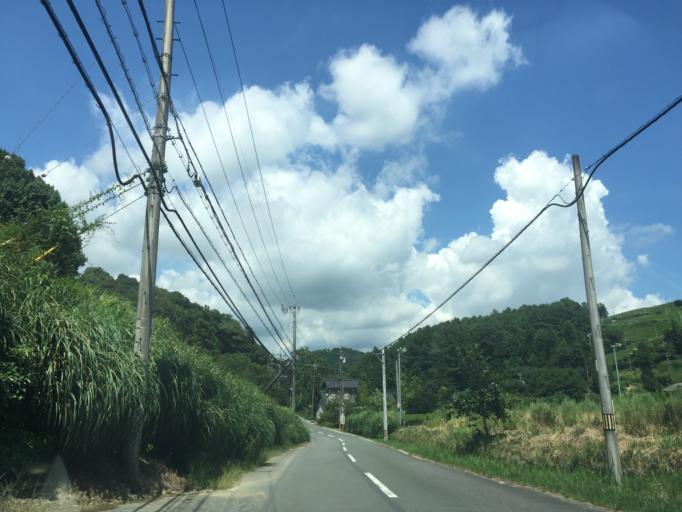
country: JP
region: Shizuoka
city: Kanaya
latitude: 34.8183
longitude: 138.0666
